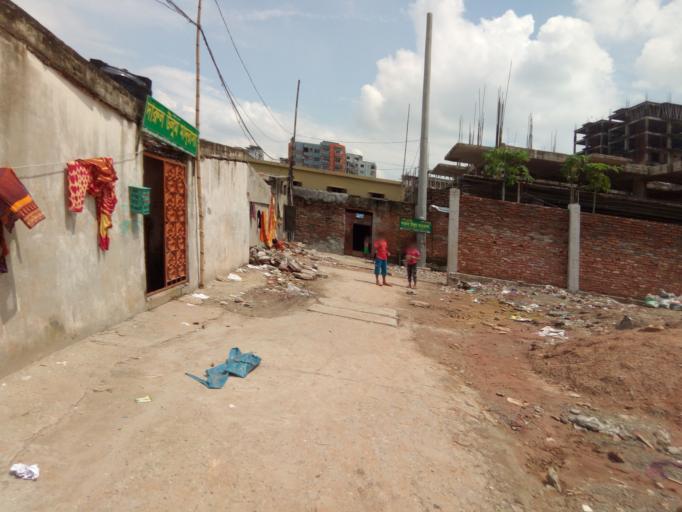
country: BD
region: Dhaka
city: Azimpur
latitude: 23.7436
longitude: 90.3616
